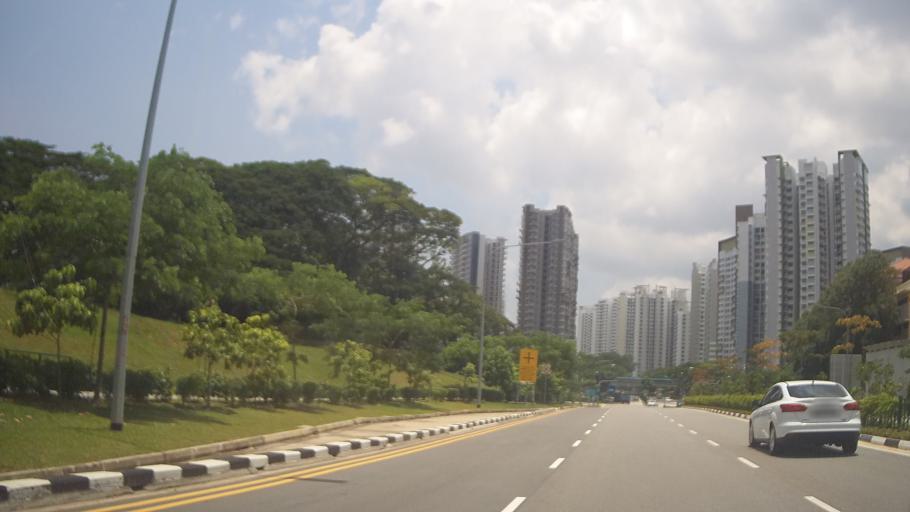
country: MY
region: Johor
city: Kampung Pasir Gudang Baru
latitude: 1.3953
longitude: 103.8712
